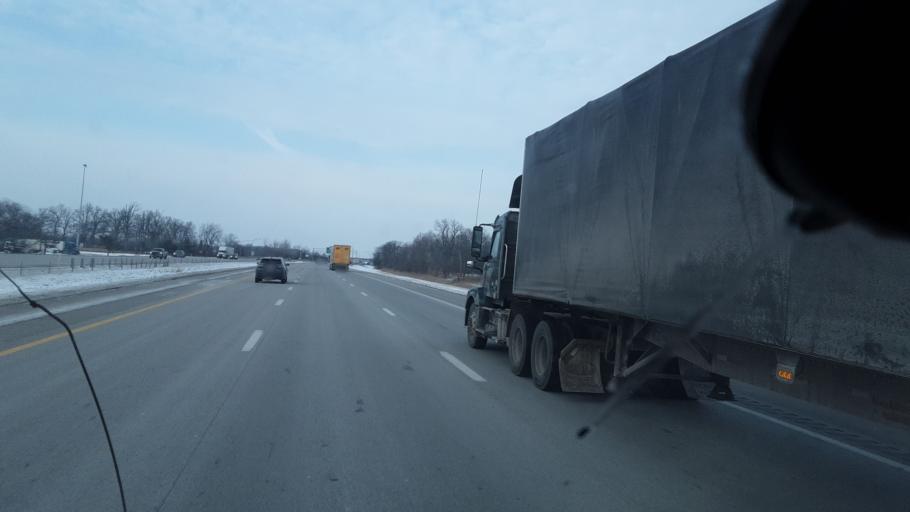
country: US
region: Ohio
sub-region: Wood County
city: Bowling Green
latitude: 41.3336
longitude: -83.6254
